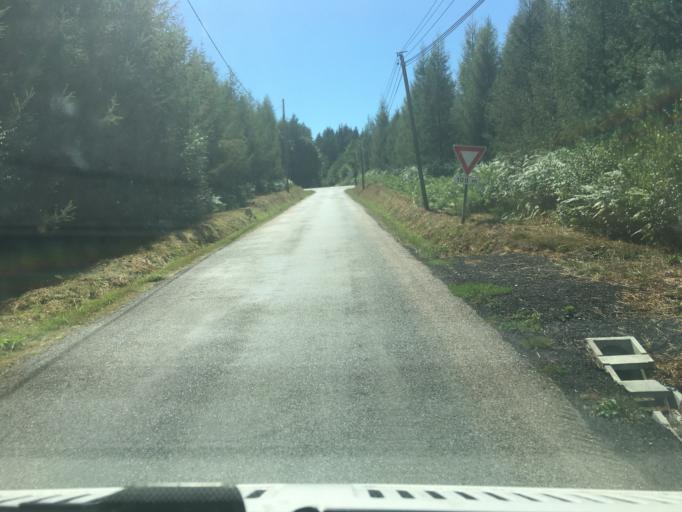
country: FR
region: Limousin
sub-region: Departement de la Correze
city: Bort-les-Orgues
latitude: 45.4343
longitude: 2.4535
